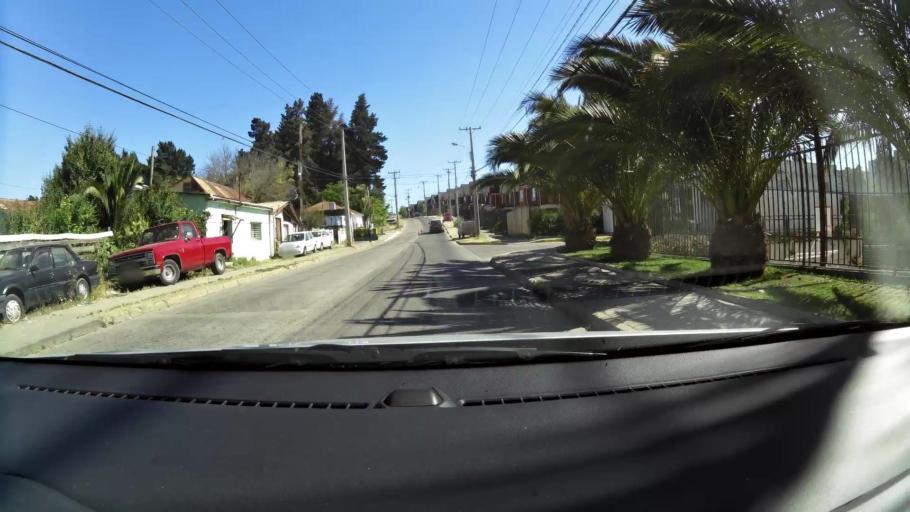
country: CL
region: Valparaiso
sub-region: Provincia de Valparaiso
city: Valparaiso
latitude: -33.0621
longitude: -71.5863
